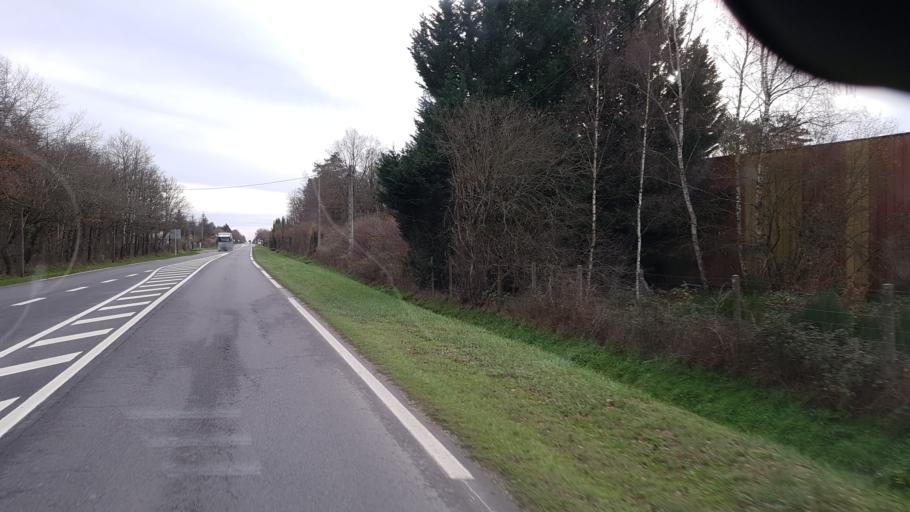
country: FR
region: Centre
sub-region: Departement du Loir-et-Cher
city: Theillay
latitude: 47.3135
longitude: 2.0576
